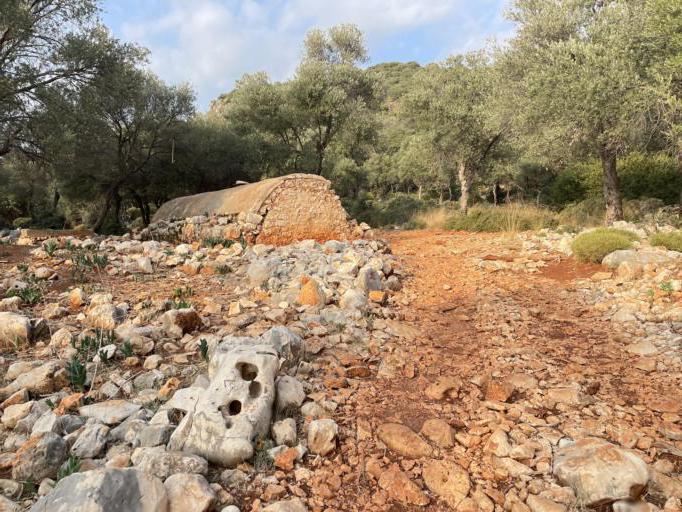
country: TR
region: Antalya
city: Kas
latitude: 36.1611
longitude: 29.6559
